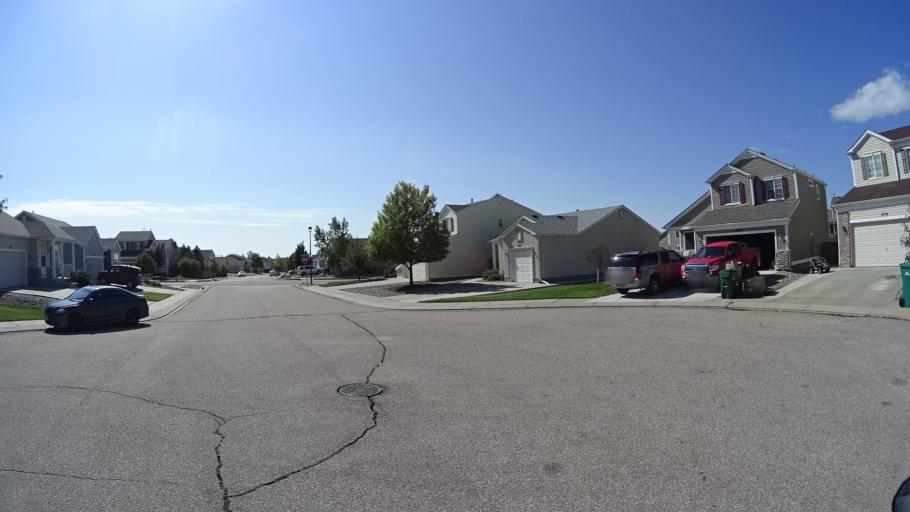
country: US
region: Colorado
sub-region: El Paso County
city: Cimarron Hills
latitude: 38.9295
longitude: -104.6991
